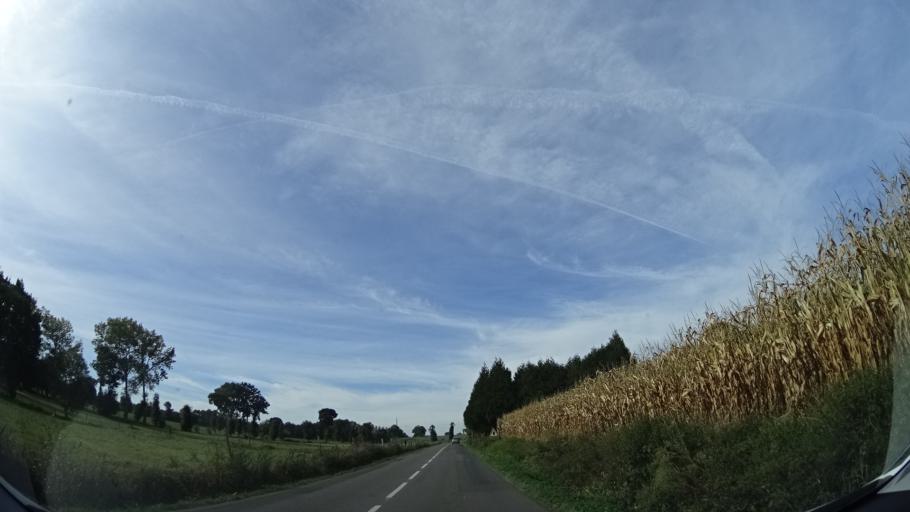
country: FR
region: Brittany
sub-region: Departement d'Ille-et-Vilaine
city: Melesse
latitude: 48.2167
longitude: -1.7218
